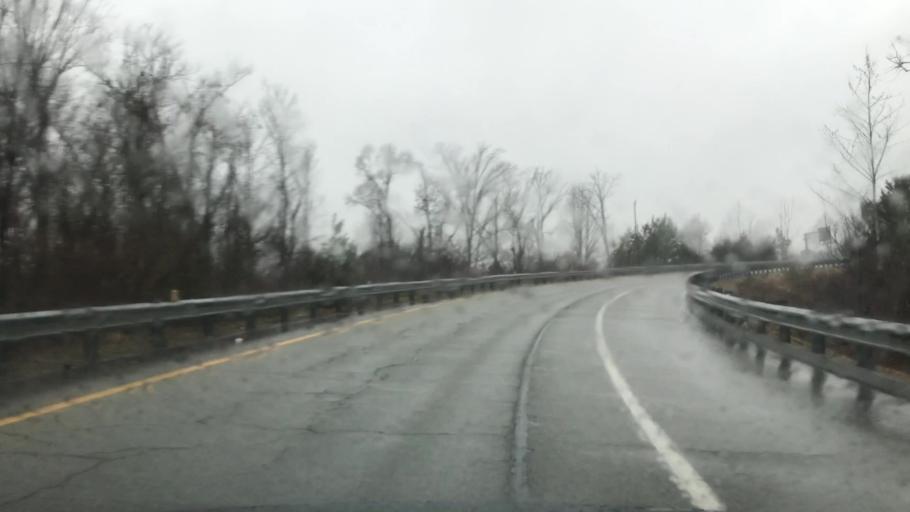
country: US
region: Virginia
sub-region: Henrico County
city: Short Pump
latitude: 37.6617
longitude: -77.6562
